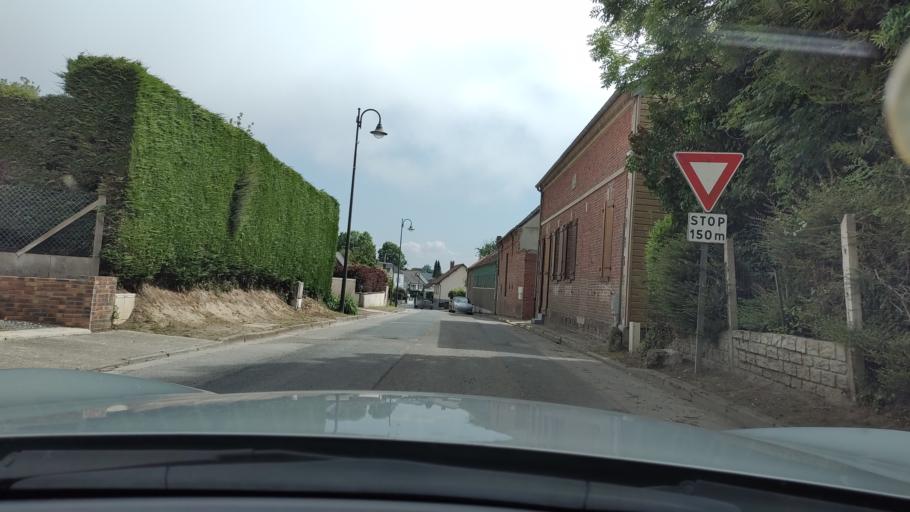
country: FR
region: Picardie
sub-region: Departement de la Somme
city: Ault
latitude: 50.0762
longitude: 1.4573
